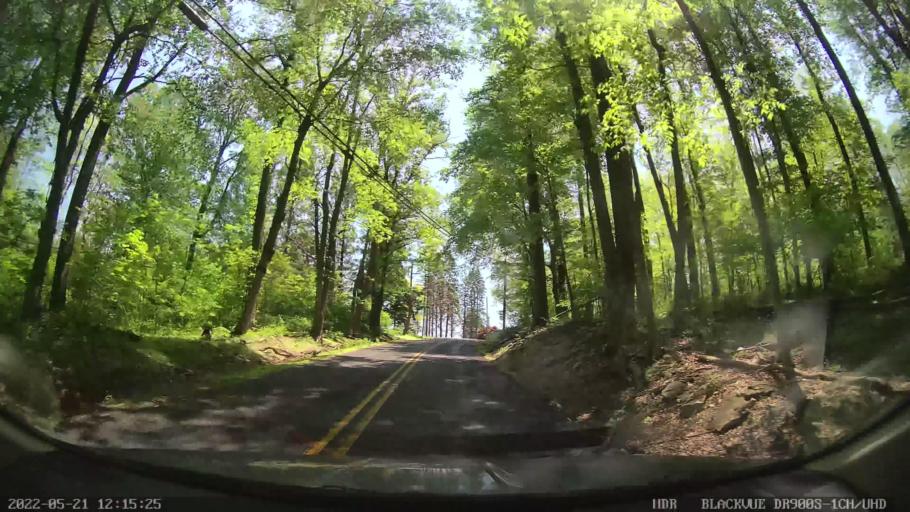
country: US
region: Pennsylvania
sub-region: Berks County
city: Red Lion
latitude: 40.4299
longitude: -75.6640
